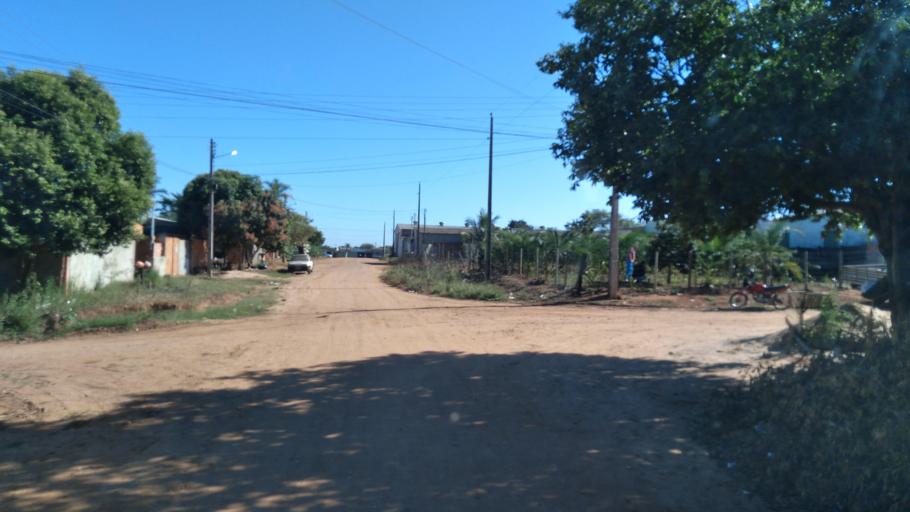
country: BR
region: Goias
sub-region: Mineiros
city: Mineiros
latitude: -17.5903
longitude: -52.5573
